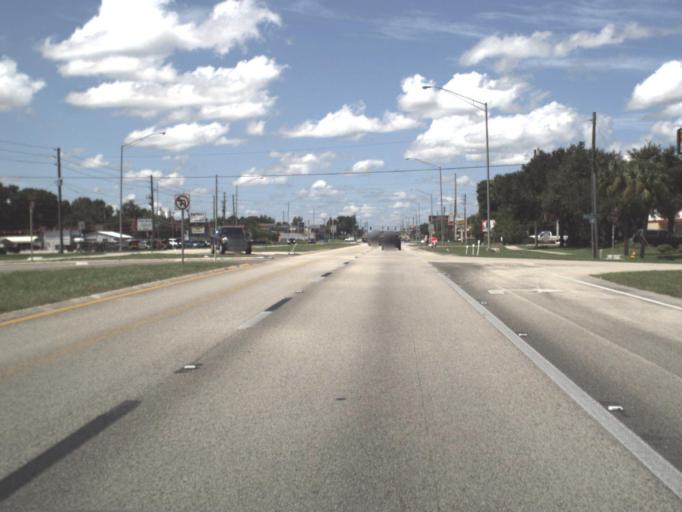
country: US
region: Florida
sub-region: Polk County
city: Combee Settlement
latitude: 28.0480
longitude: -81.9033
